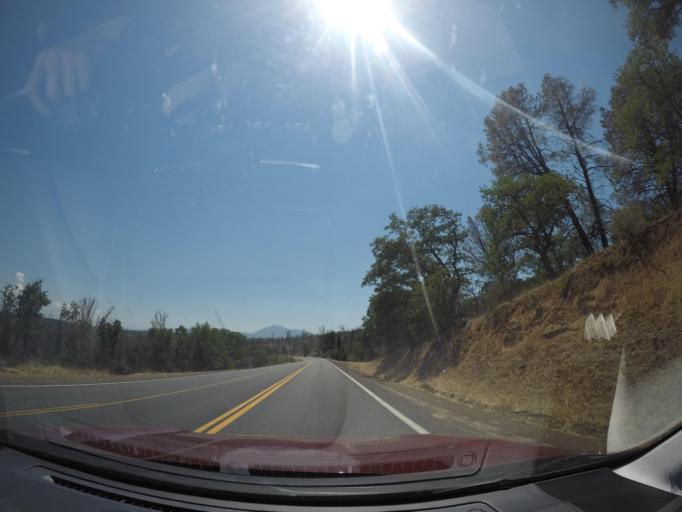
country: US
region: California
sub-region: Shasta County
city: Burney
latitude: 40.9982
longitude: -121.5103
